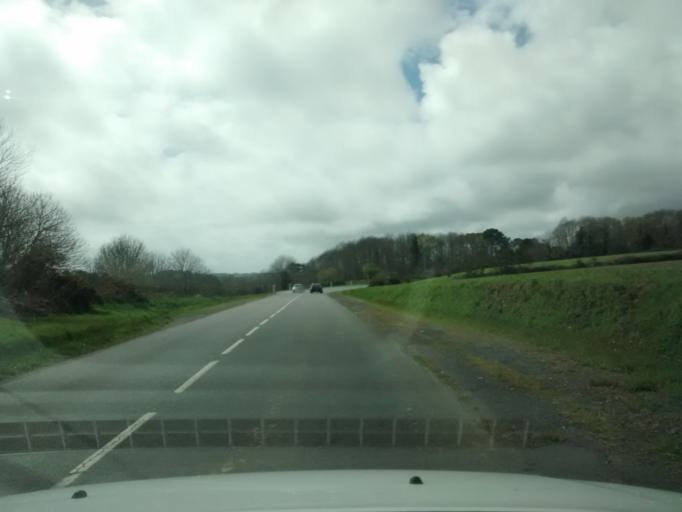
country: FR
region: Brittany
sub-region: Departement du Morbihan
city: Guidel-Plage
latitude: 47.7921
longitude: -3.5201
